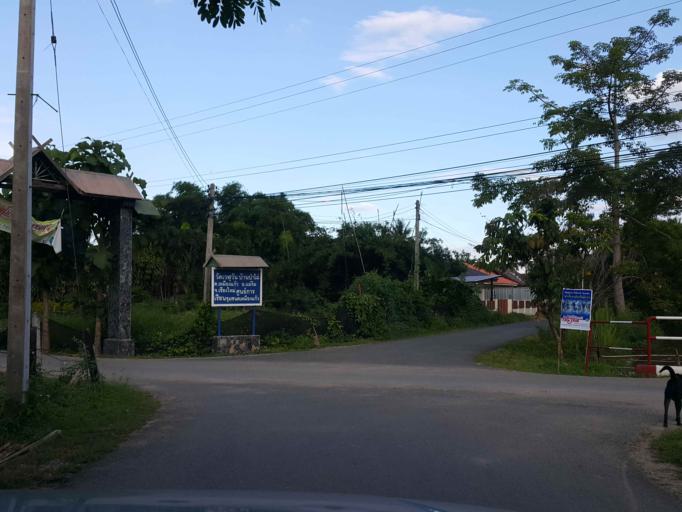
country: TH
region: Chiang Mai
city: San Sai
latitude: 18.9007
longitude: 98.9778
